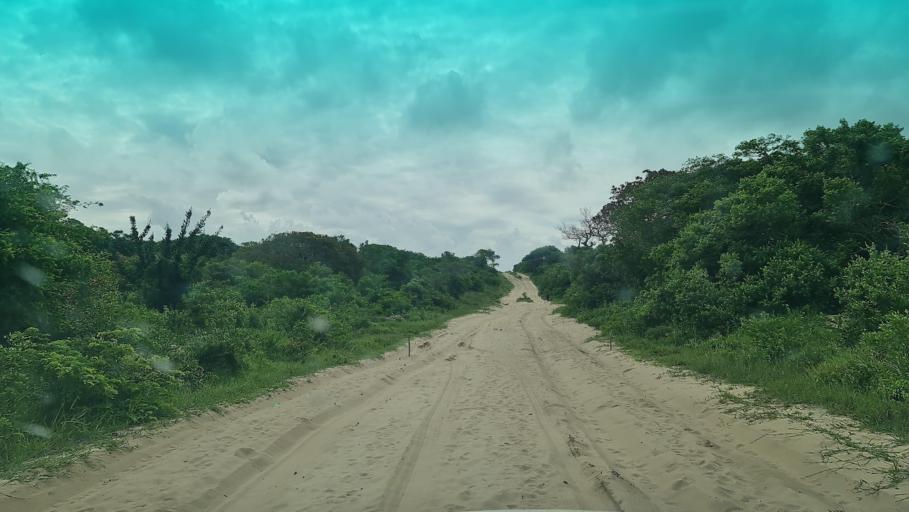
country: MZ
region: Maputo
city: Manhica
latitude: -25.4412
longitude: 32.9316
